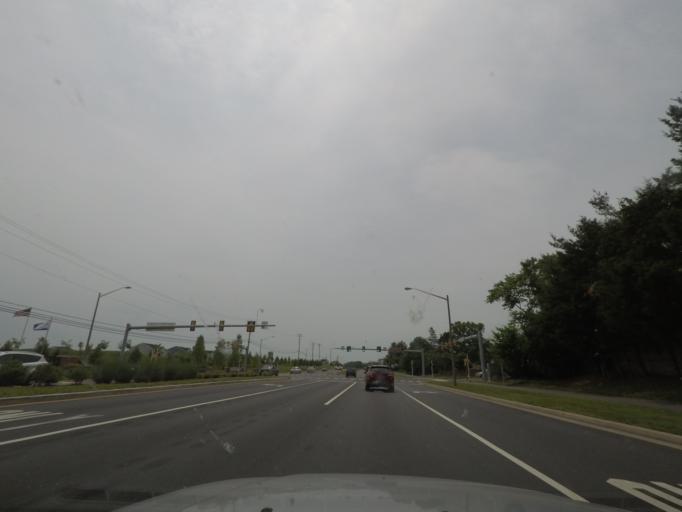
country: US
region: Virginia
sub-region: Loudoun County
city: Leesburg
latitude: 39.0974
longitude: -77.5790
